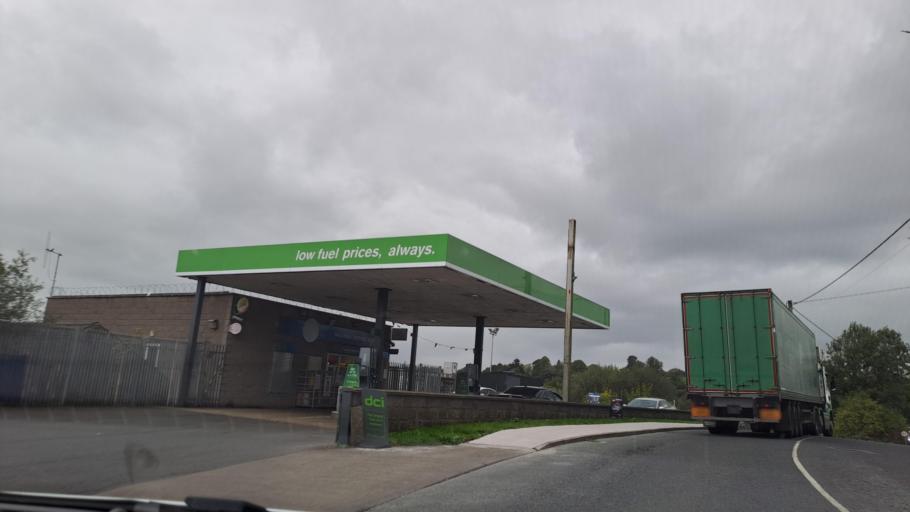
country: IE
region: Ulster
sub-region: County Monaghan
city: Monaghan
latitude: 54.1313
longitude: -6.9043
